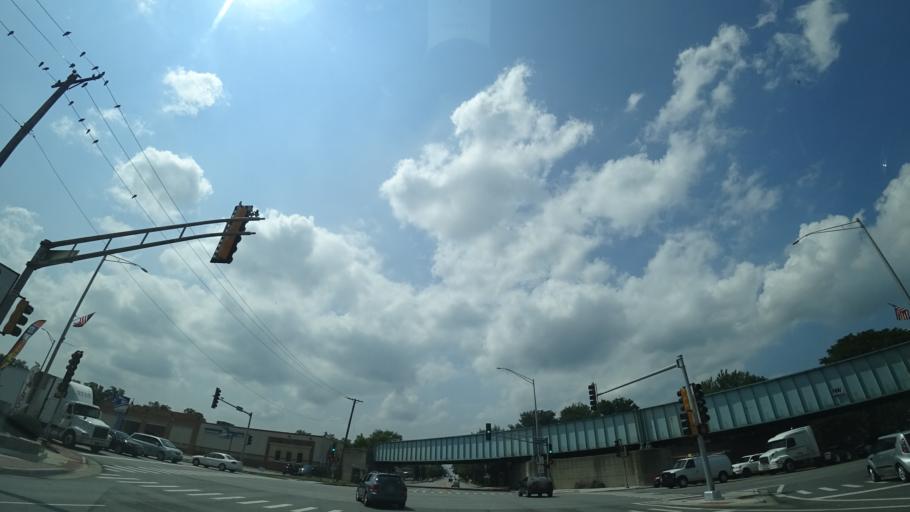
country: US
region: Illinois
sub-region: Cook County
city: Worth
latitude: 41.6899
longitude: -87.7971
